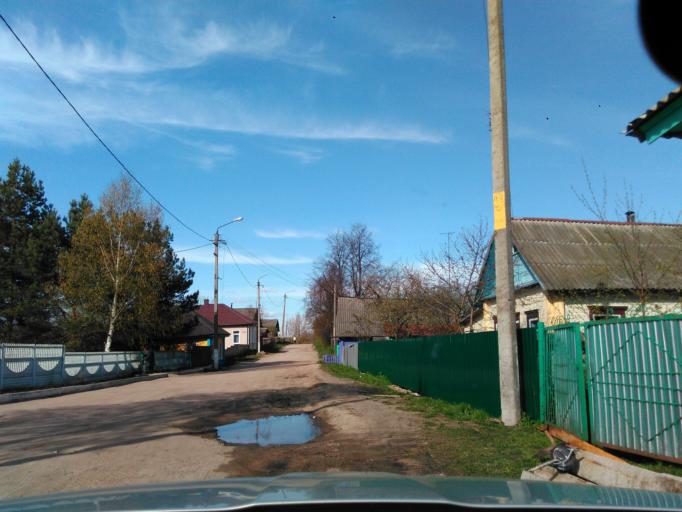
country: BY
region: Vitebsk
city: Chashniki
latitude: 54.8620
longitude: 29.1643
